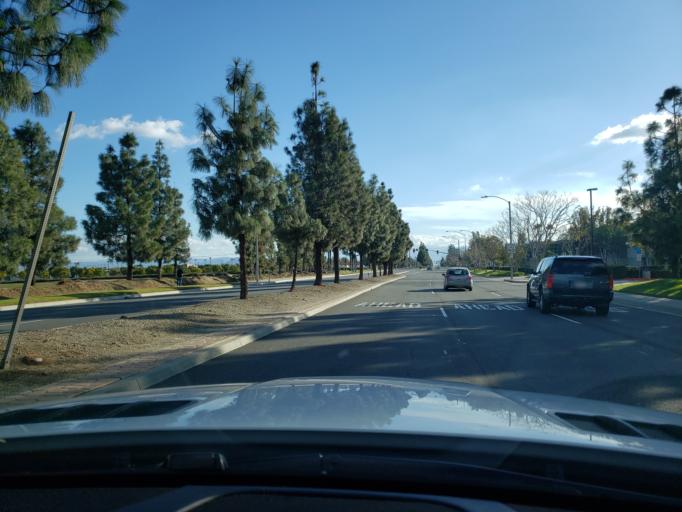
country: US
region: California
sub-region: Riverside County
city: Mira Loma
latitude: 34.0470
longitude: -117.5583
